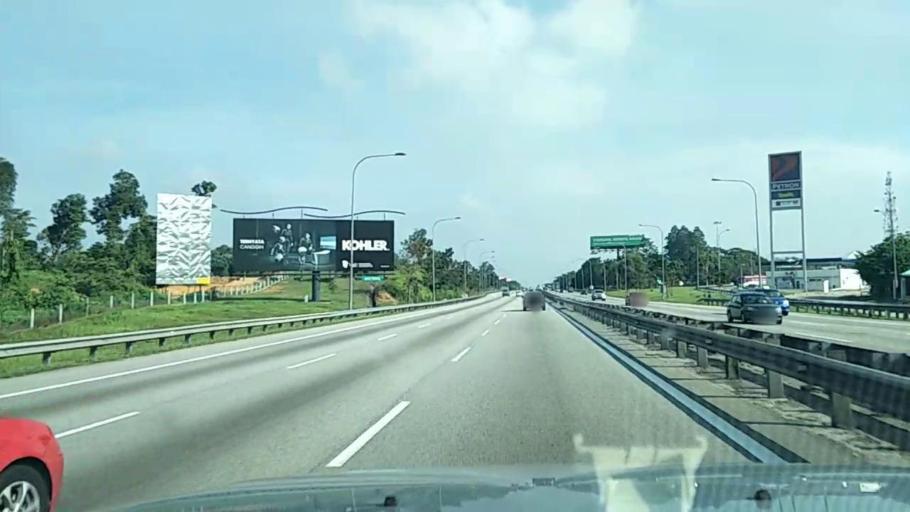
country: MY
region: Putrajaya
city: Putrajaya
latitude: 2.8998
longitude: 101.6159
